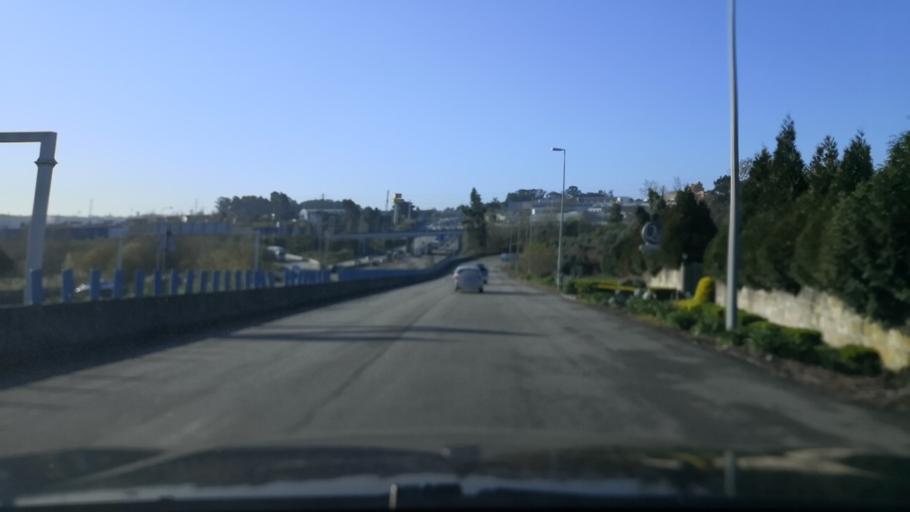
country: PT
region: Porto
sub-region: Maia
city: Leca do Bailio
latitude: 41.2056
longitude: -8.6278
